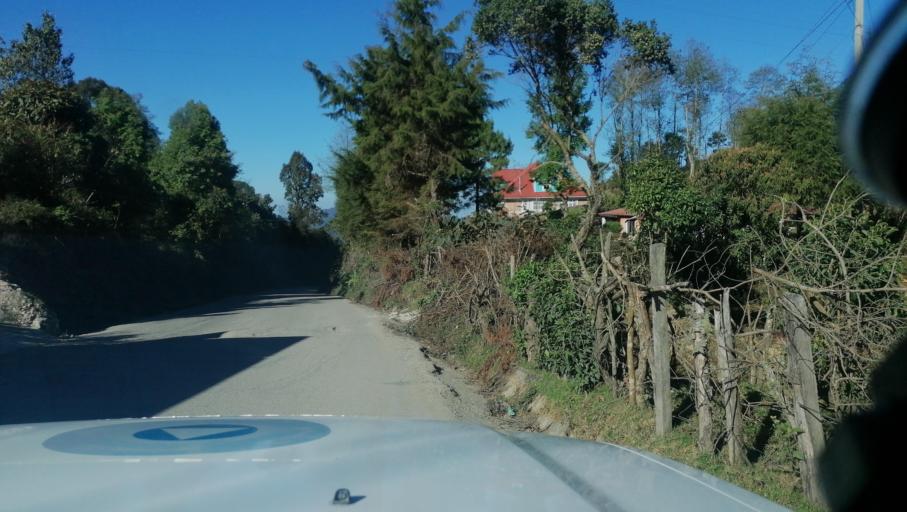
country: MX
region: Chiapas
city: Motozintla de Mendoza
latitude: 15.2736
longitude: -92.2318
